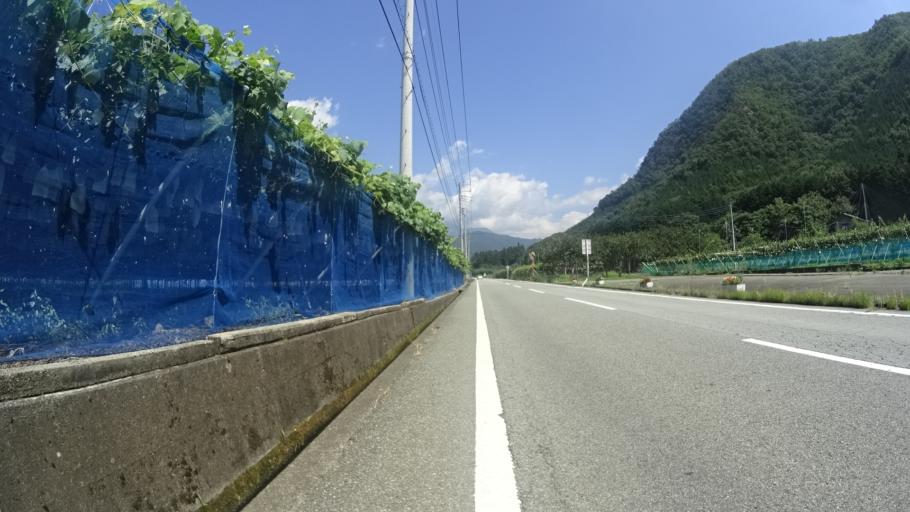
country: JP
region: Yamanashi
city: Enzan
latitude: 35.7318
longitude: 138.7223
